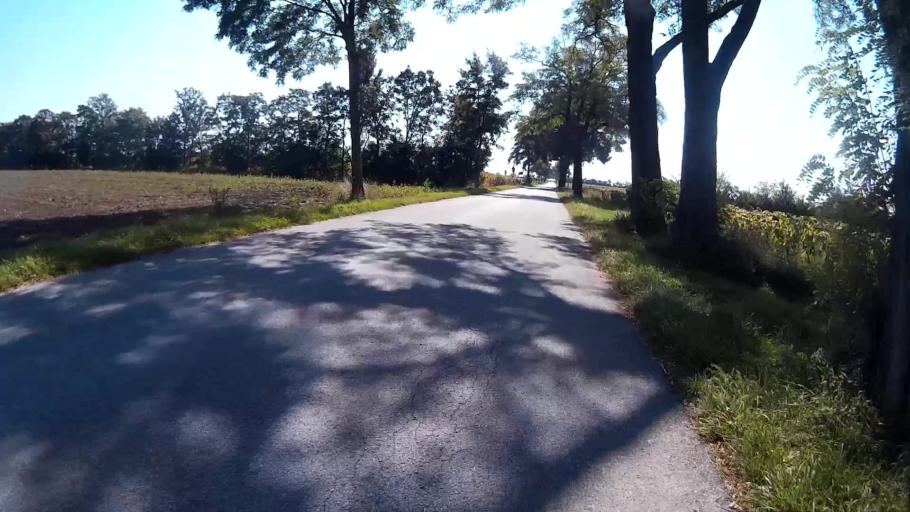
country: CZ
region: South Moravian
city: Novosedly
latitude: 48.7835
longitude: 16.4921
